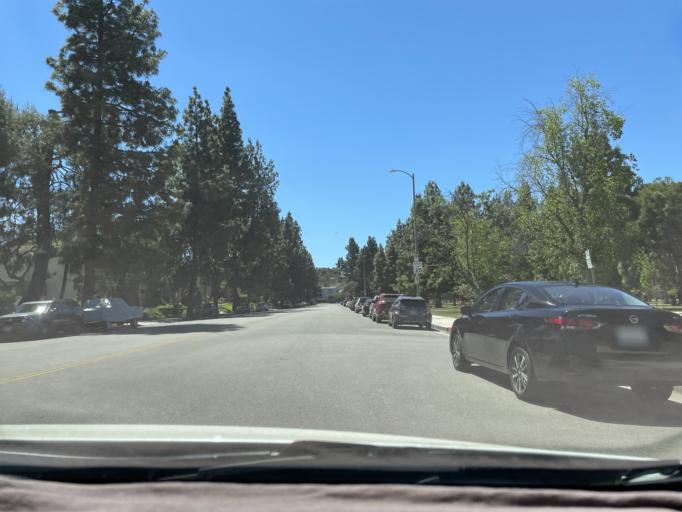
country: US
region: California
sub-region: Los Angeles County
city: Woodland Hills
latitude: 34.1754
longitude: -118.6020
